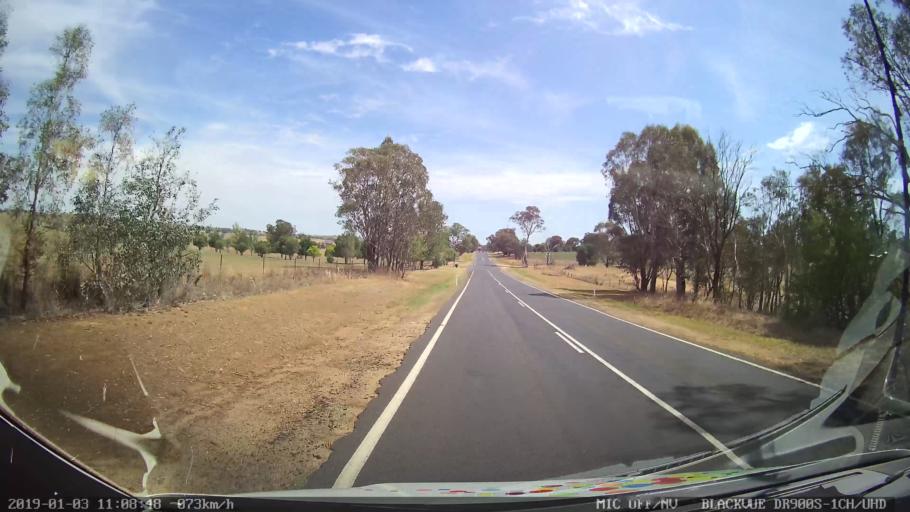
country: AU
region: New South Wales
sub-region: Young
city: Young
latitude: -34.2456
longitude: 148.2558
